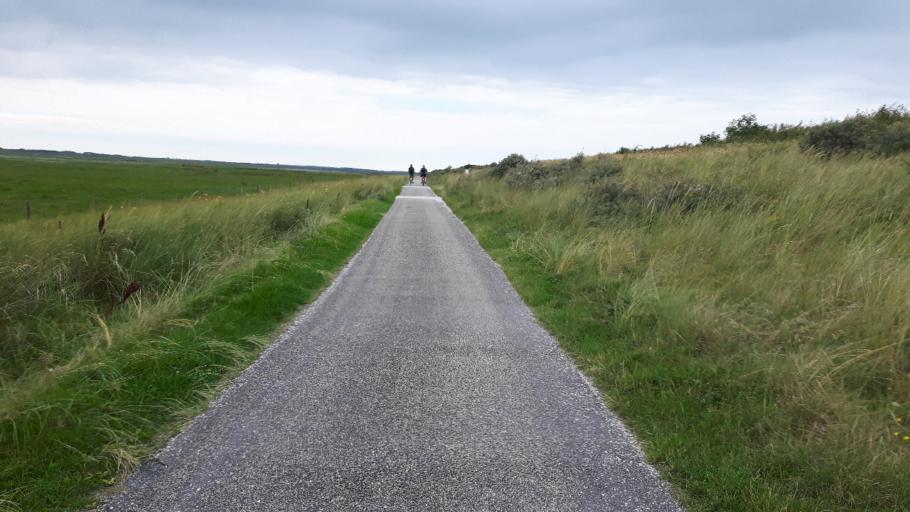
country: NL
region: Friesland
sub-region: Gemeente Dongeradeel
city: Holwerd
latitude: 53.4603
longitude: 5.8799
